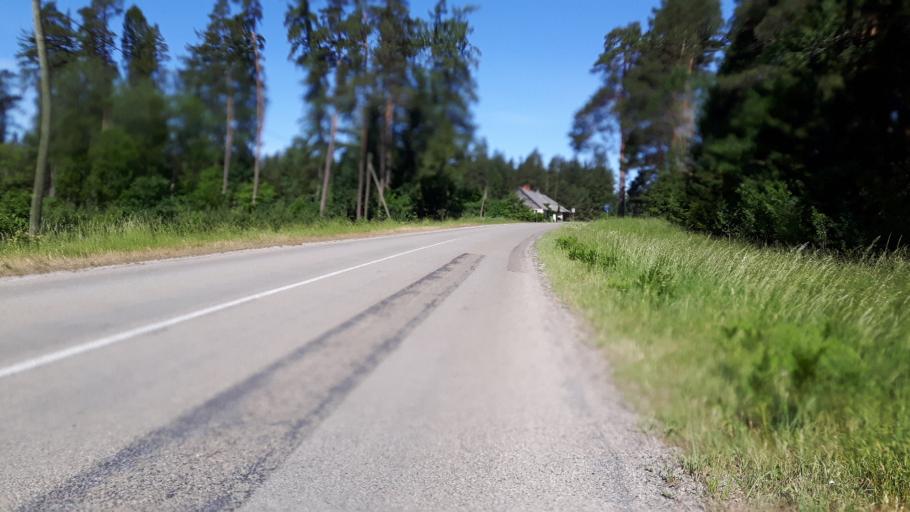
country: LV
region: Tukuma Rajons
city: Tukums
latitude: 57.0110
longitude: 23.0530
